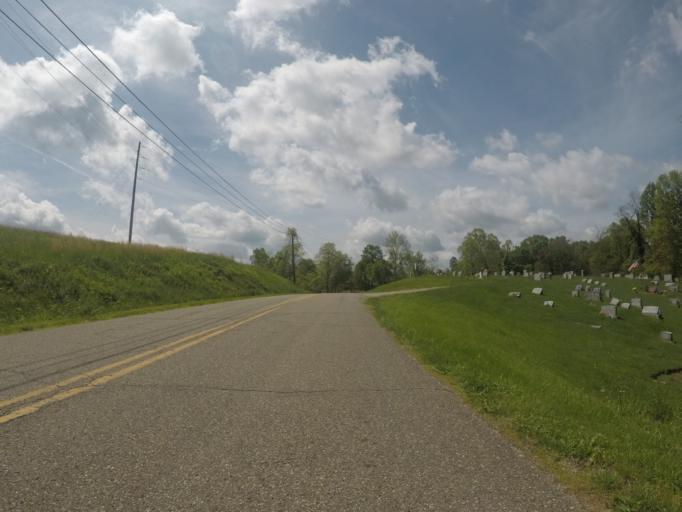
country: US
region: West Virginia
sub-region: Cabell County
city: Huntington
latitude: 38.5452
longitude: -82.4312
